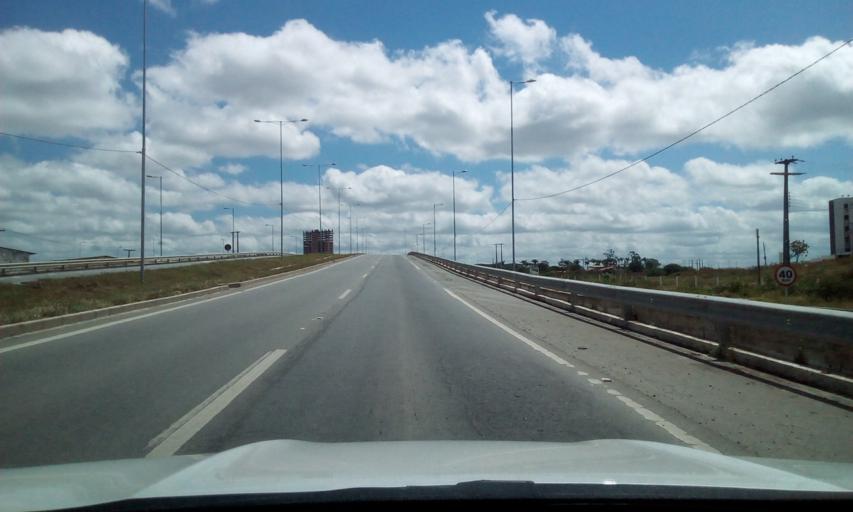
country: BR
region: Paraiba
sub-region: Campina Grande
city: Campina Grande
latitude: -7.2583
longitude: -35.8775
